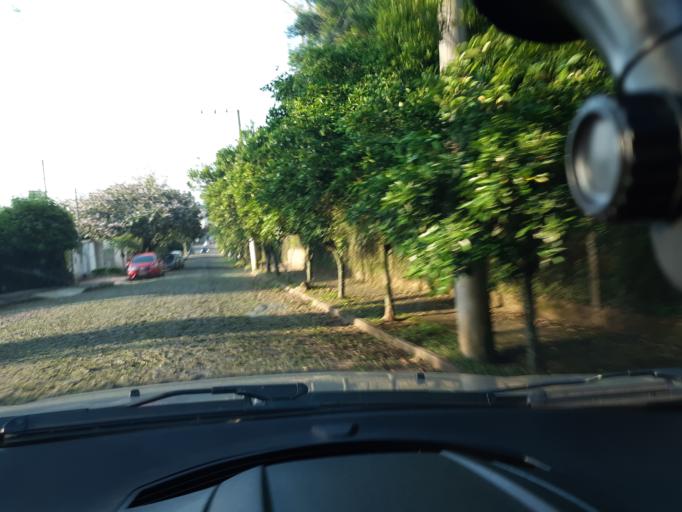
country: BR
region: Rio Grande do Sul
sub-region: Sao Leopoldo
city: Sao Leopoldo
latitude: -29.7749
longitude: -51.1401
